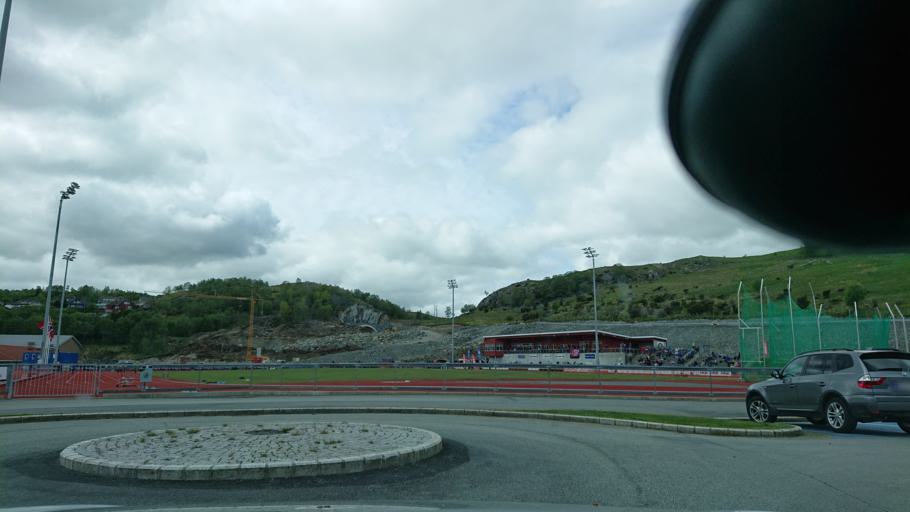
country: NO
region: Rogaland
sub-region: Gjesdal
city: Algard
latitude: 58.7756
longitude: 5.8665
